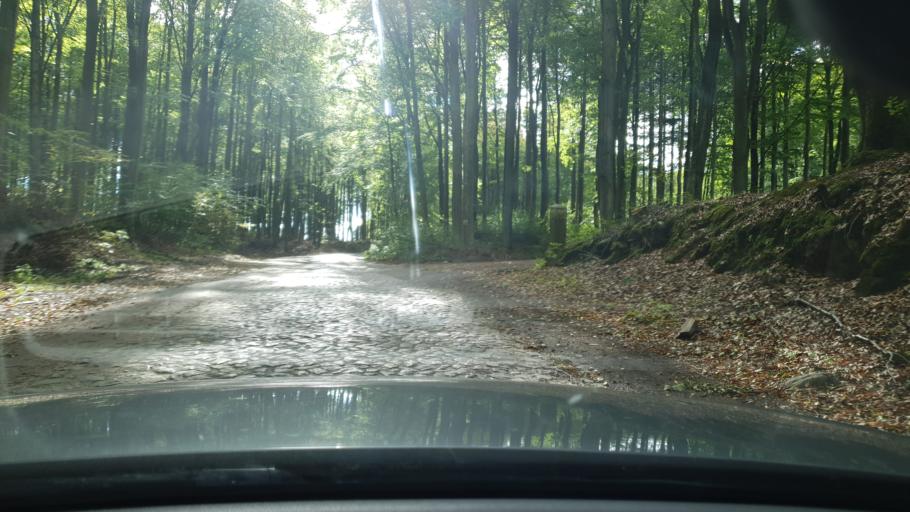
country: PL
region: Pomeranian Voivodeship
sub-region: Powiat wejherowski
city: Reda
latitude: 54.5844
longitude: 18.3159
